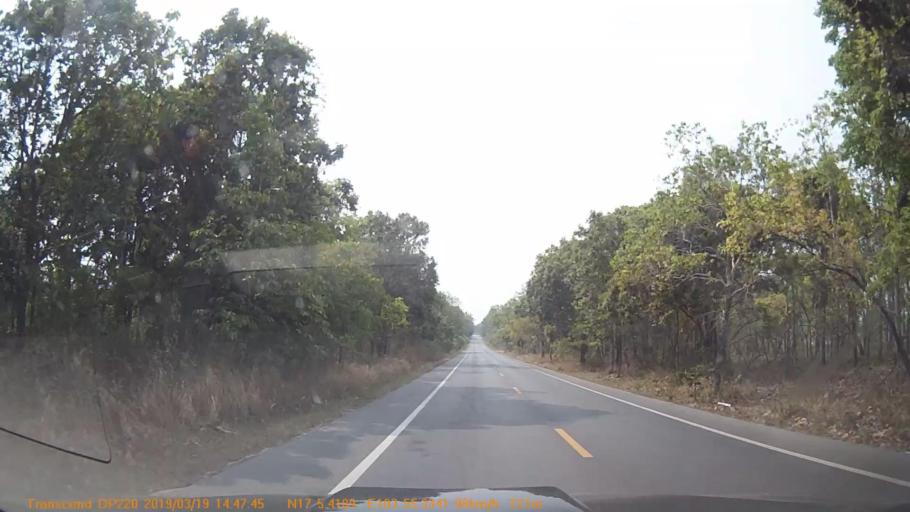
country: TH
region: Sakon Nakhon
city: Kut Bak
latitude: 17.0905
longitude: 103.9220
